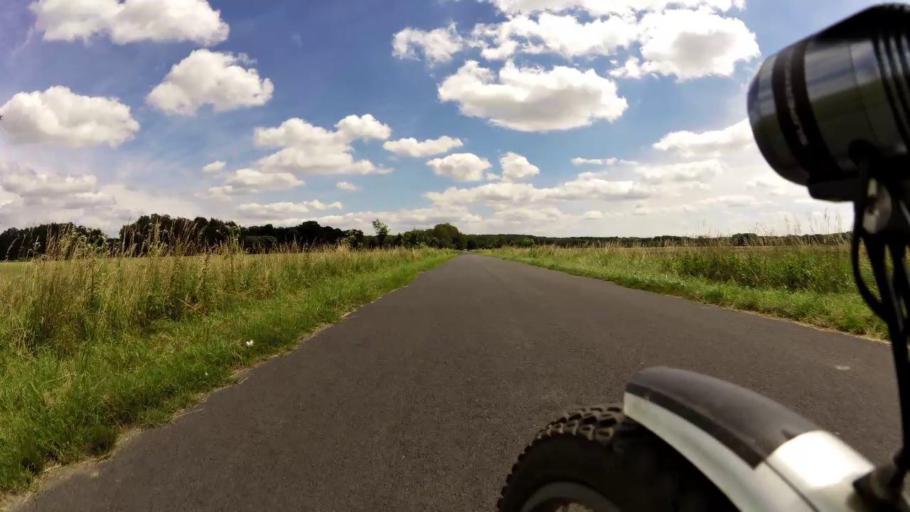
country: PL
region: West Pomeranian Voivodeship
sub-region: Powiat choszczenski
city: Choszczno
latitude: 53.2273
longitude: 15.3945
